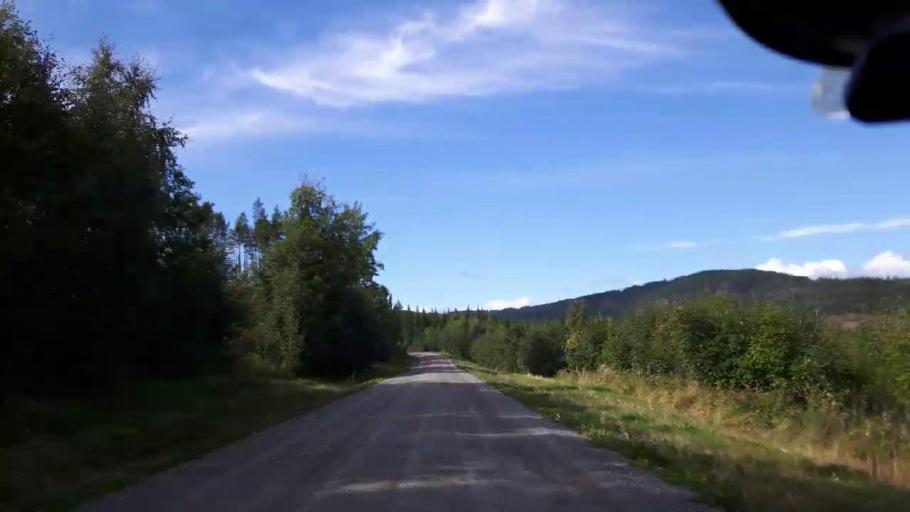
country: SE
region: Jaemtland
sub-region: Ragunda Kommun
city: Hammarstrand
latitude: 63.1350
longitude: 16.1115
